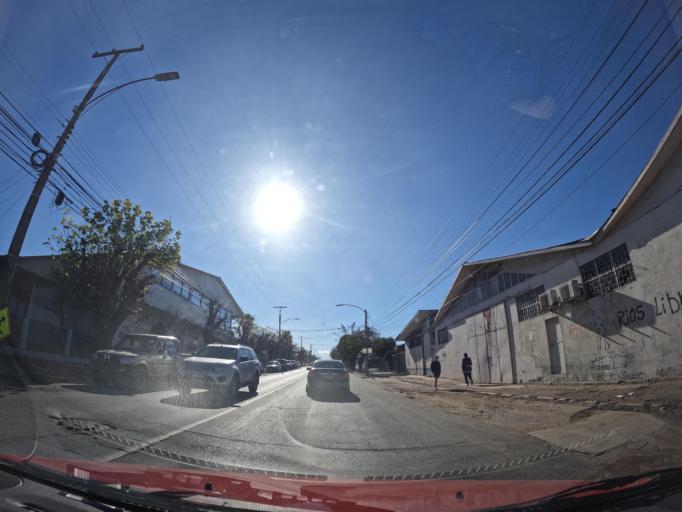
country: CL
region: Maule
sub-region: Provincia de Cauquenes
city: Cauquenes
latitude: -35.9722
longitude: -72.3149
